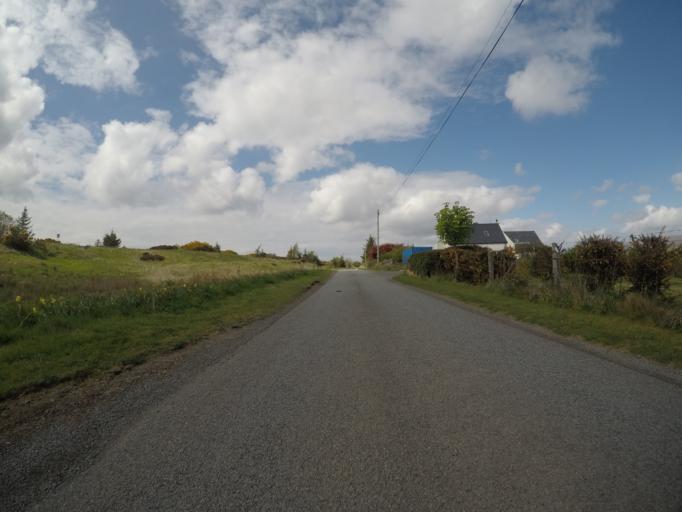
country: GB
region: Scotland
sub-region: Highland
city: Isle of Skye
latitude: 57.4633
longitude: -6.3317
